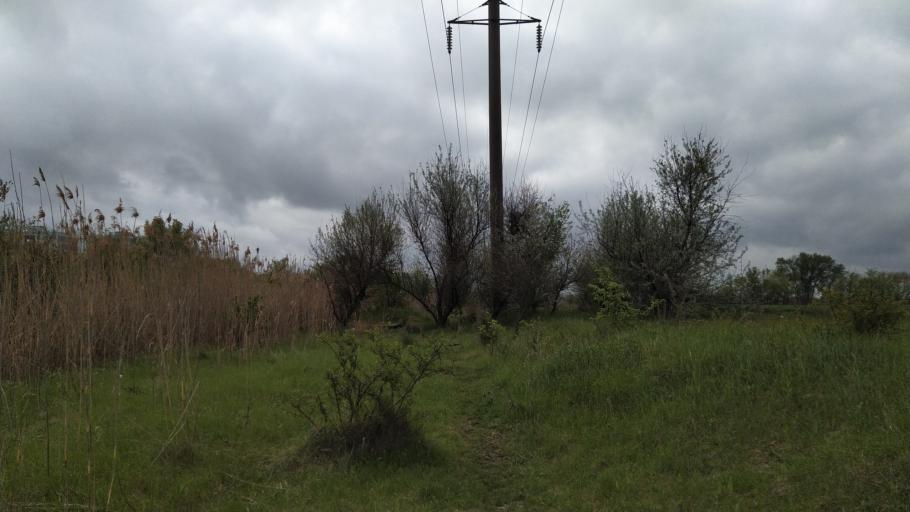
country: RU
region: Rostov
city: Bataysk
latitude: 47.1229
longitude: 39.7310
